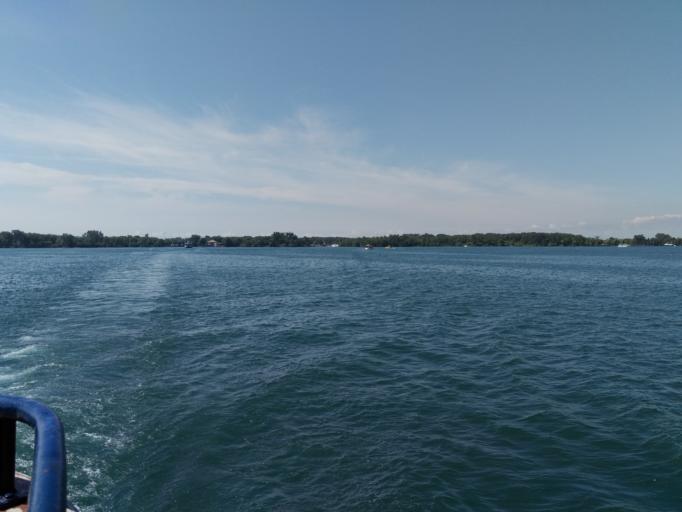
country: CA
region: Ontario
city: Toronto
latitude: 43.6330
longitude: -79.3721
